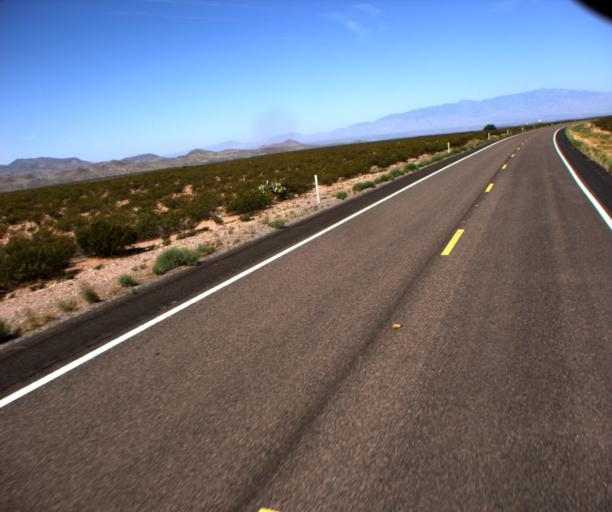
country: US
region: Arizona
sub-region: Greenlee County
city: Clifton
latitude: 32.7517
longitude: -109.3400
